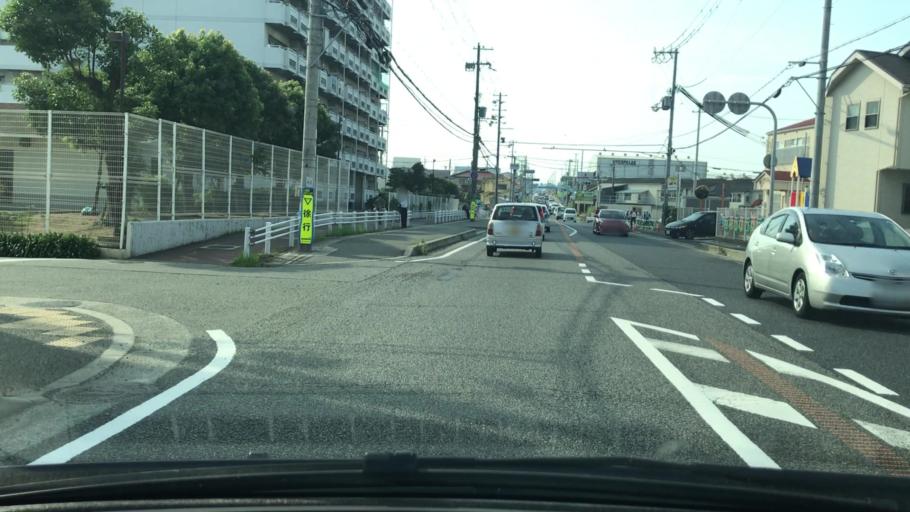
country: JP
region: Hyogo
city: Kakogawacho-honmachi
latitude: 34.7126
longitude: 134.9011
